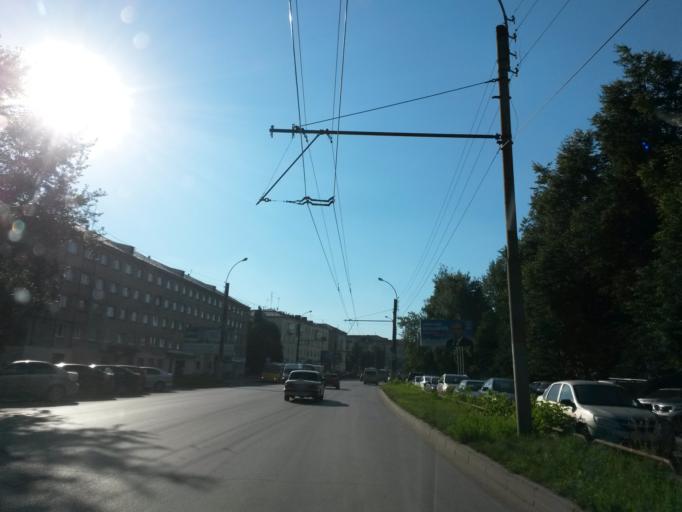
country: RU
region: Ivanovo
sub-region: Gorod Ivanovo
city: Ivanovo
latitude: 56.9835
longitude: 40.9638
